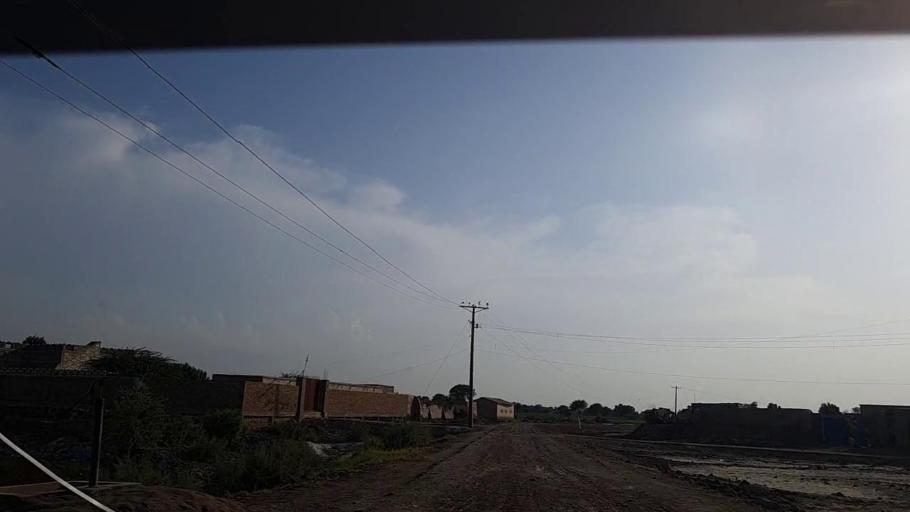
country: PK
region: Sindh
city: Khanpur
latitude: 27.8306
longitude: 69.3779
